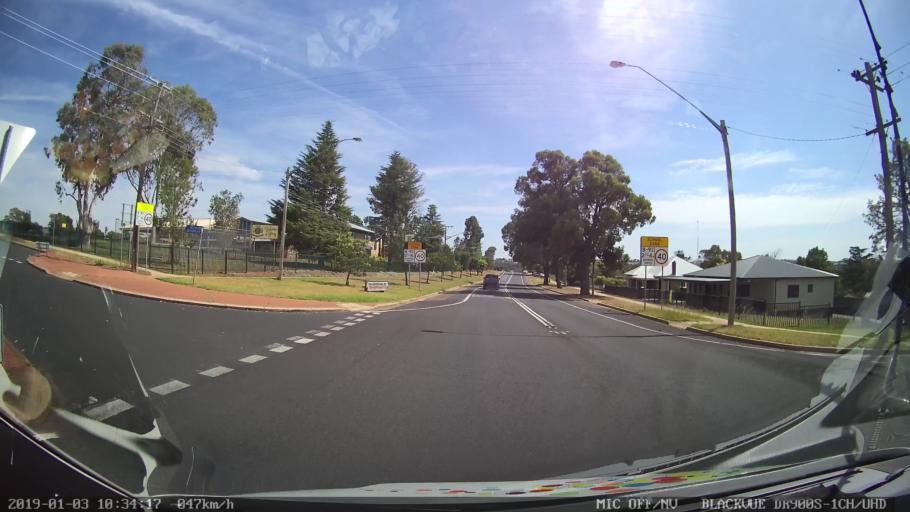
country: AU
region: New South Wales
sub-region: Young
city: Young
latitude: -34.3226
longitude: 148.2910
